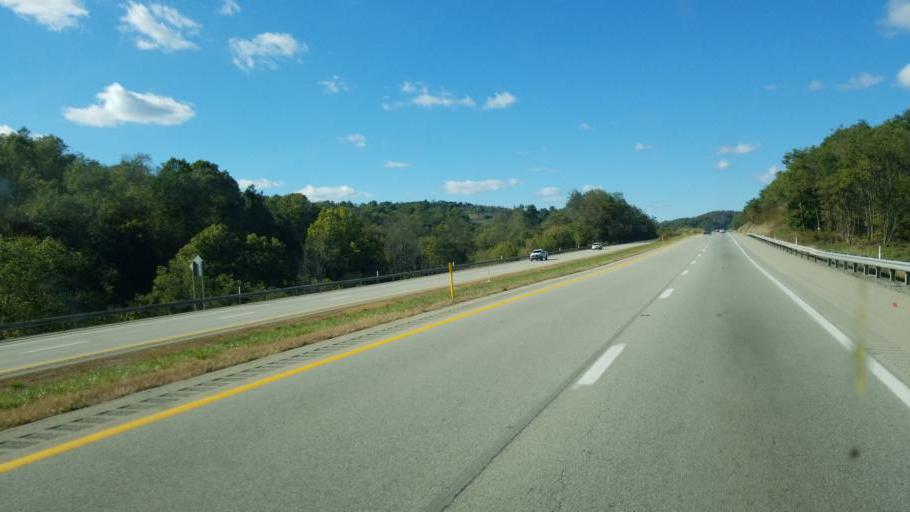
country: US
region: Pennsylvania
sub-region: Greene County
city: Waynesburg
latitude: 39.9812
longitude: -80.1805
